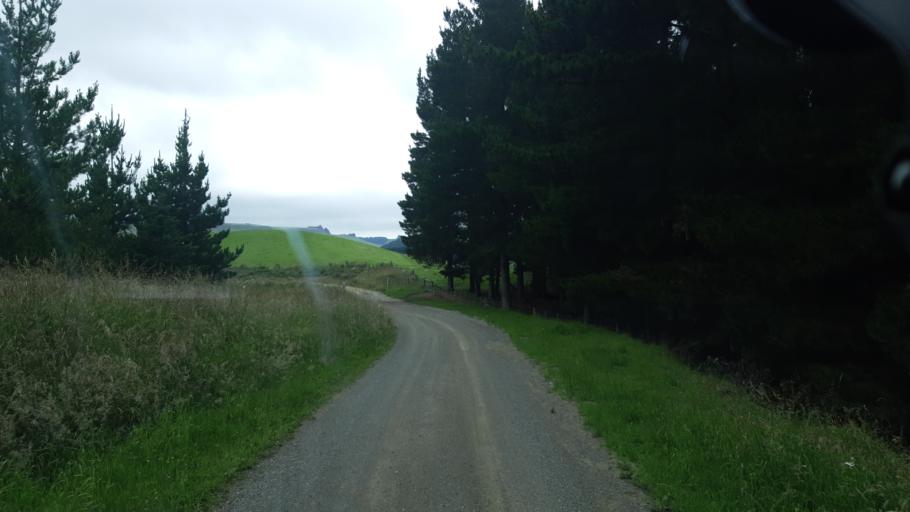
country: NZ
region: Canterbury
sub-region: Timaru District
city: Pleasant Point
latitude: -44.3467
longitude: 171.0409
